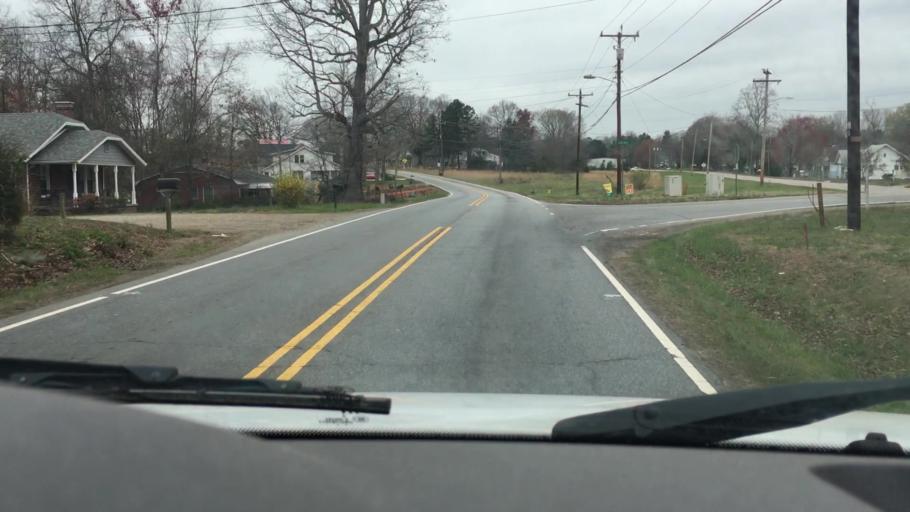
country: US
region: North Carolina
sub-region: Iredell County
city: Troutman
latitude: 35.6940
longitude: -80.8738
